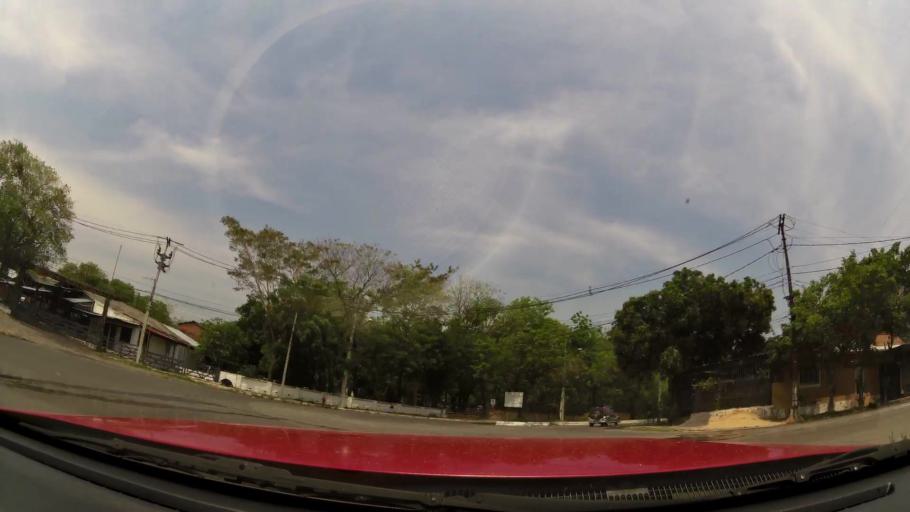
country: PY
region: Asuncion
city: Asuncion
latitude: -25.2665
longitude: -57.5973
